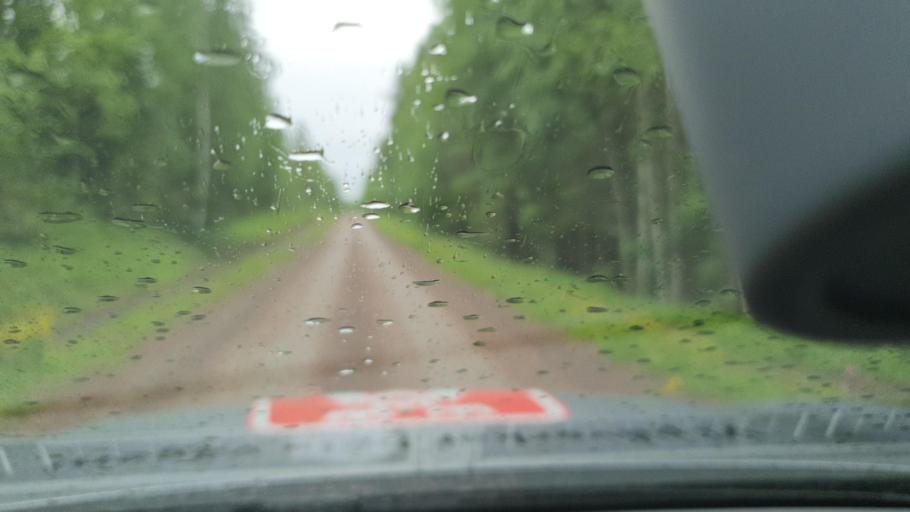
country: SE
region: Norrbotten
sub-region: Overkalix Kommun
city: OEverkalix
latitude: 66.5283
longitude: 22.7413
